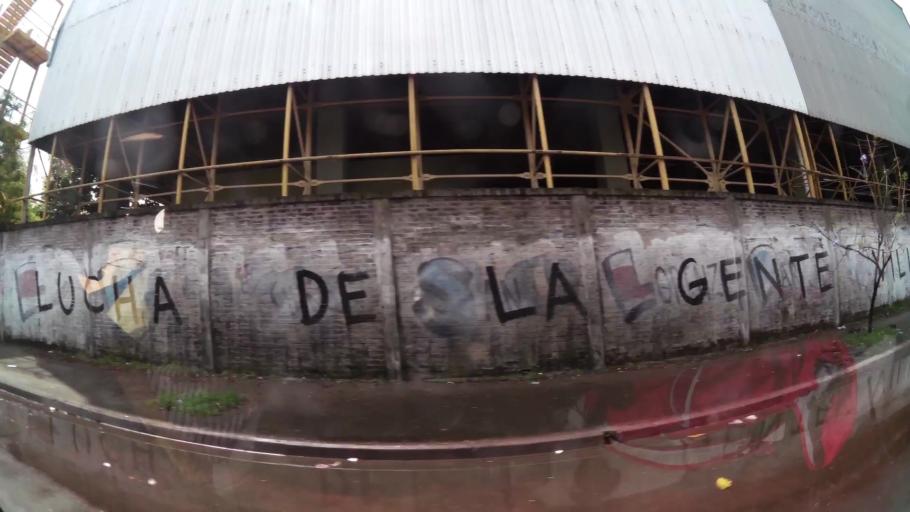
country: AR
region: Buenos Aires F.D.
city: Villa Lugano
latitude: -34.6506
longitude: -58.4564
